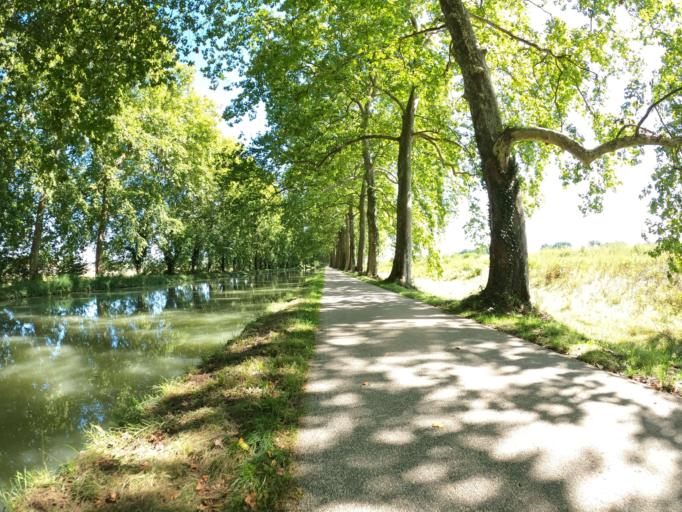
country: FR
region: Midi-Pyrenees
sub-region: Departement du Tarn-et-Garonne
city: Auvillar
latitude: 44.0945
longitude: 0.9463
